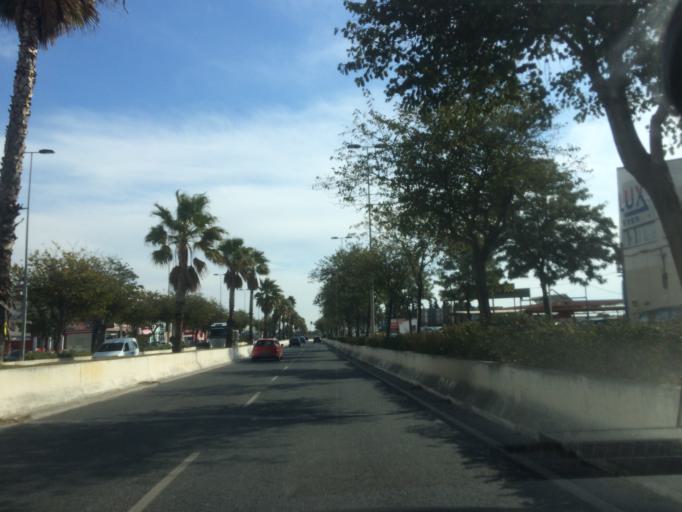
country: ES
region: Andalusia
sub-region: Provincia de Malaga
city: Torremolinos
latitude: 36.6602
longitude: -4.4978
